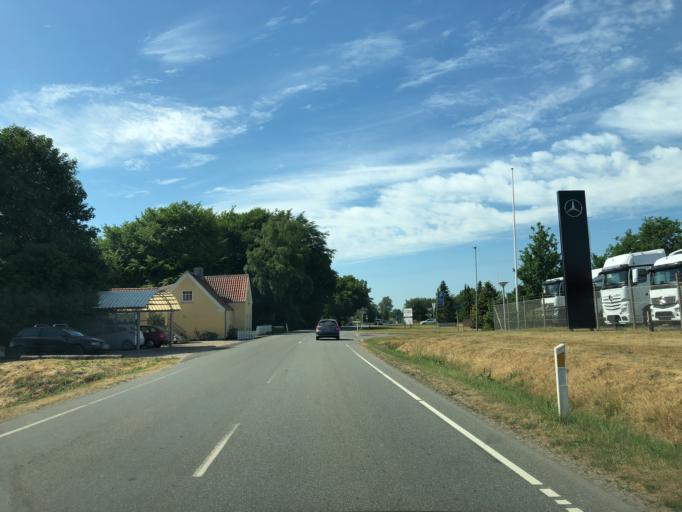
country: DK
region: Central Jutland
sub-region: Ikast-Brande Kommune
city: Brande
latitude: 55.9315
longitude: 9.1458
